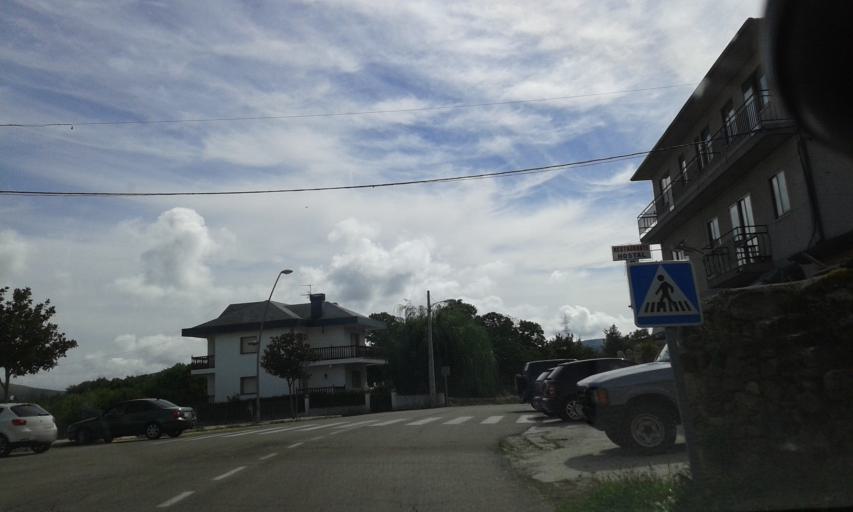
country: ES
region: Galicia
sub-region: Provincia de Ourense
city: Manzaneda
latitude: 42.3083
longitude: -7.2323
